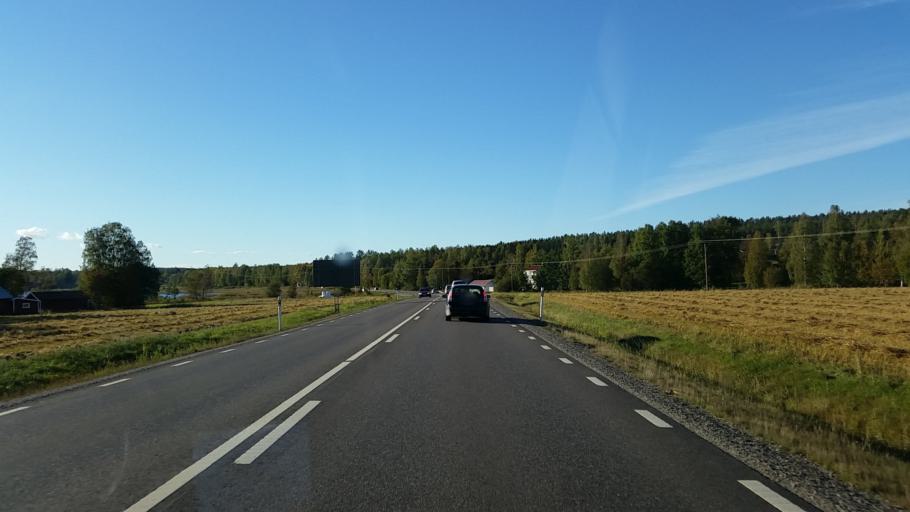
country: SE
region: Gaevleborg
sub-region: Hudiksvalls Kommun
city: Sorforsa
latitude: 61.7308
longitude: 16.9611
